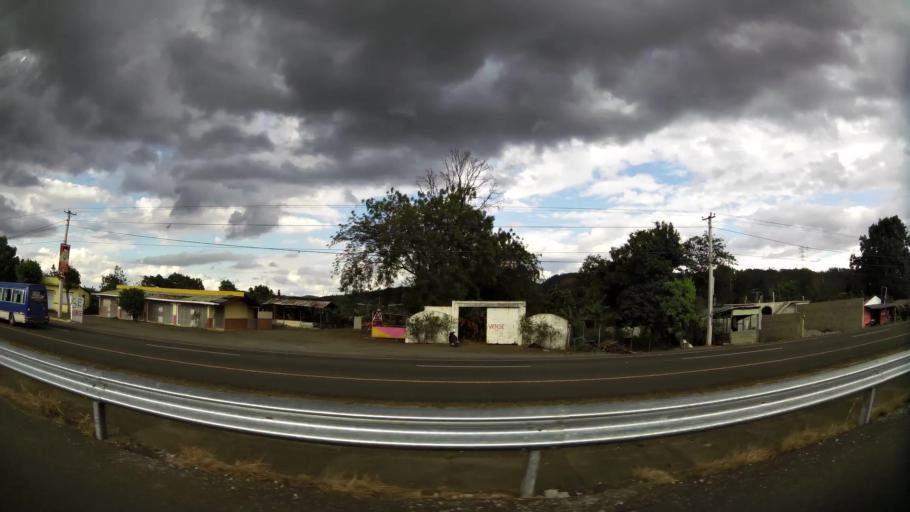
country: DO
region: Monsenor Nouel
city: Bonao
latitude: 18.9871
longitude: -70.4295
